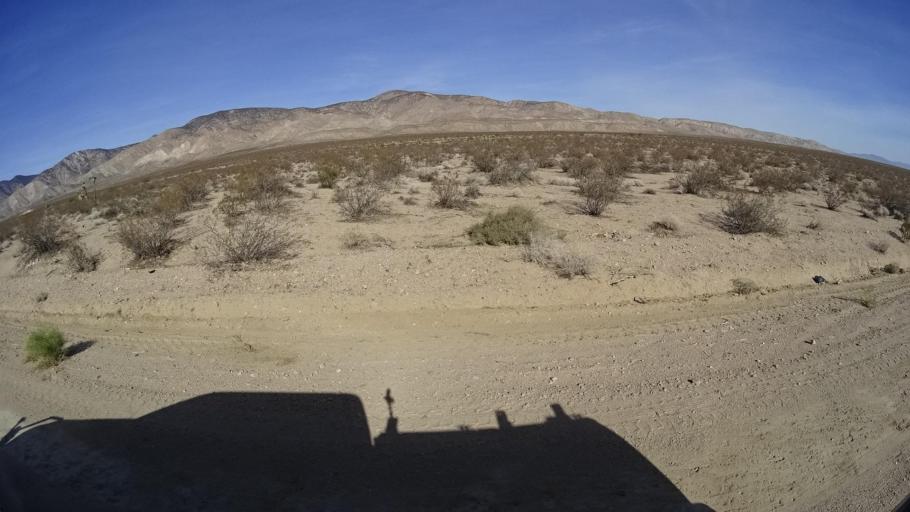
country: US
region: California
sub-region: Kern County
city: Mojave
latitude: 35.1235
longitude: -118.1763
